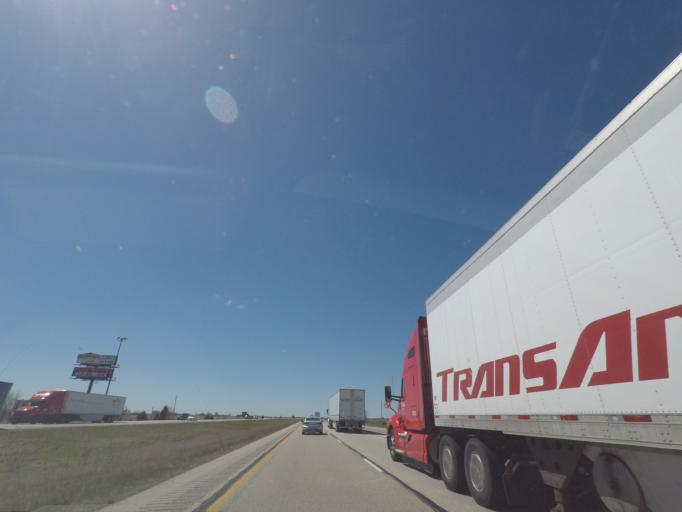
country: US
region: Illinois
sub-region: McLean County
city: Hudson
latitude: 40.5700
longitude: -88.9033
